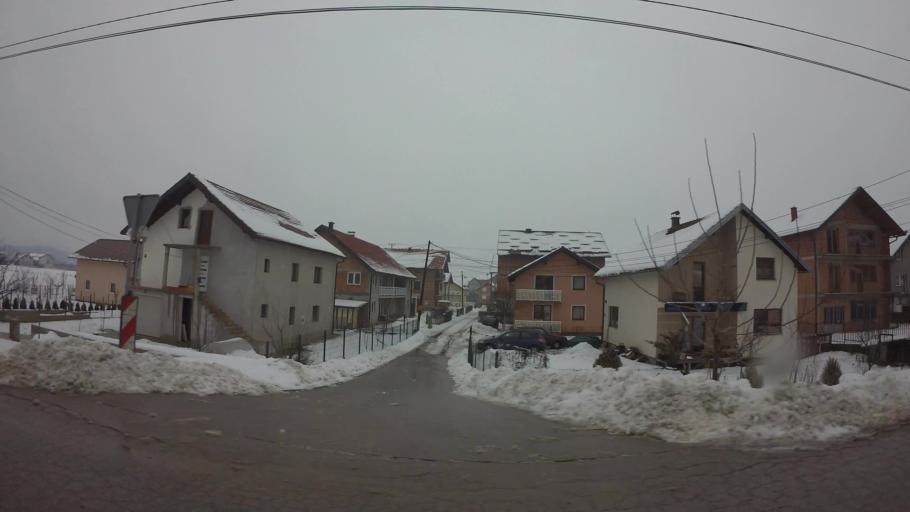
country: BA
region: Federation of Bosnia and Herzegovina
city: Hadzici
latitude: 43.8532
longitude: 18.2751
